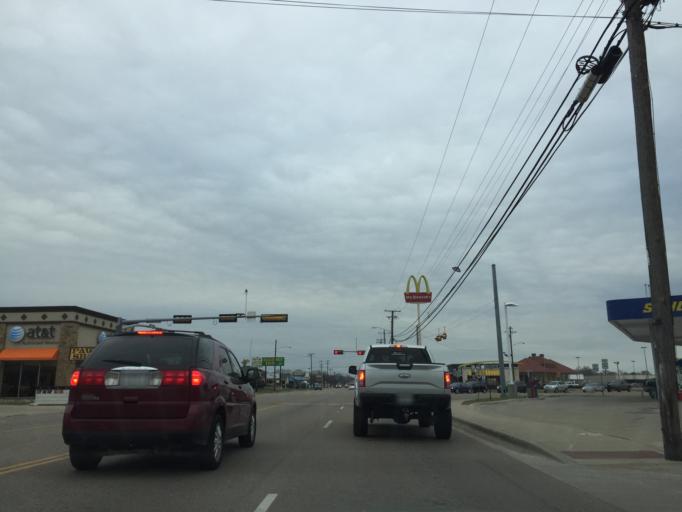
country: US
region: Texas
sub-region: Coryell County
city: Gatesville
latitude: 31.4348
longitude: -97.7330
